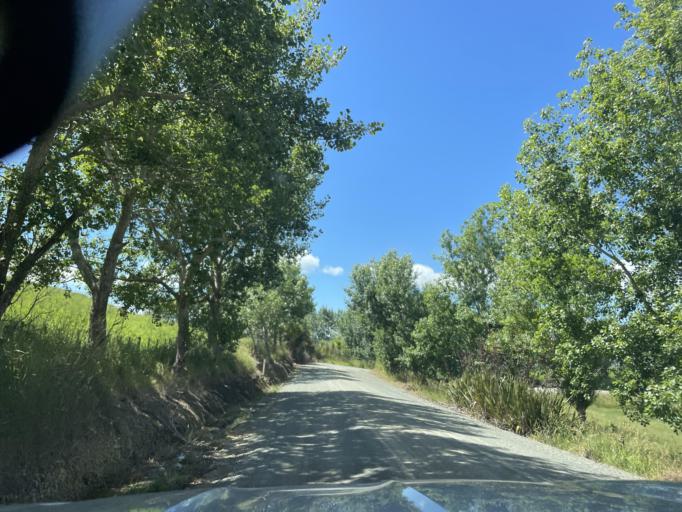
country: NZ
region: Auckland
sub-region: Auckland
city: Wellsford
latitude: -36.2732
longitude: 174.3716
